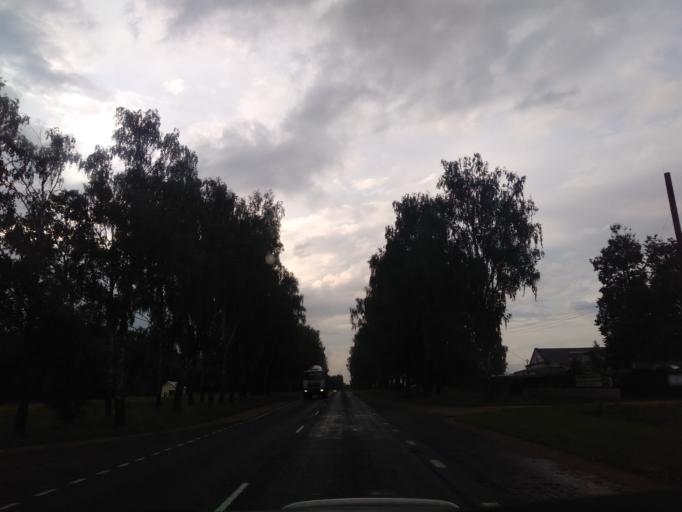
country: BY
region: Minsk
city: Uzda
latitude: 53.4960
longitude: 27.1673
